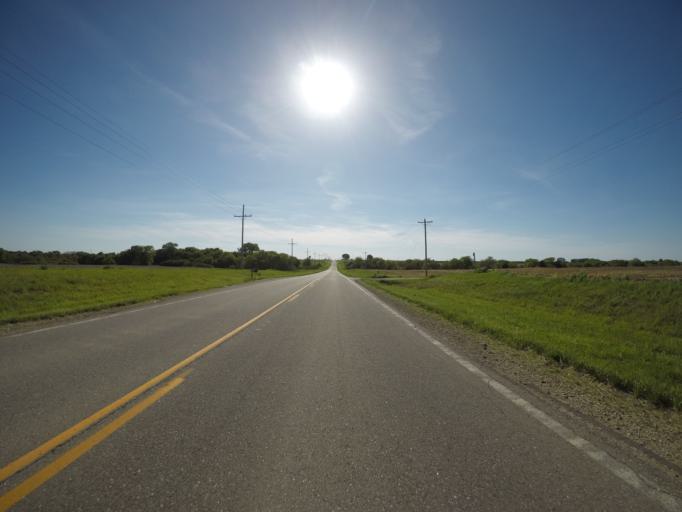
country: US
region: Kansas
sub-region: Clay County
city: Clay Center
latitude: 39.3646
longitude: -96.8818
